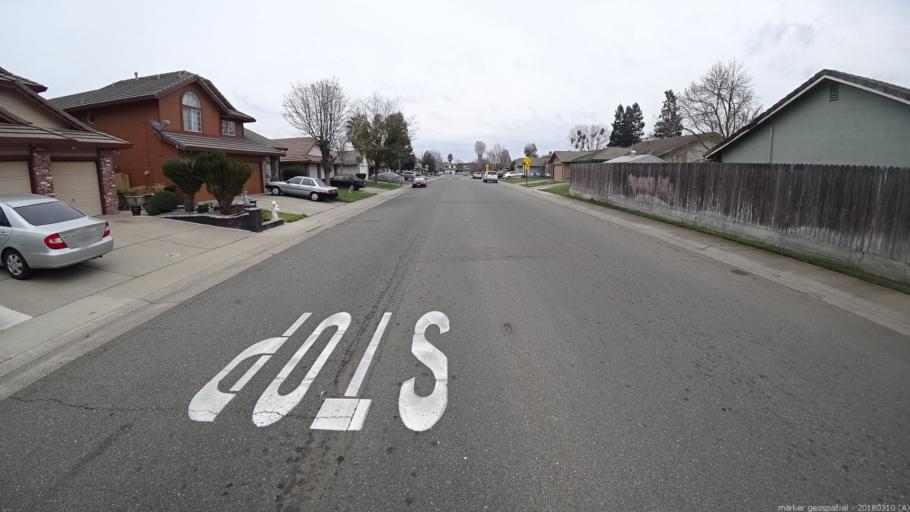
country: US
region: California
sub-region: Sacramento County
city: Vineyard
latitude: 38.4690
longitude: -121.3676
